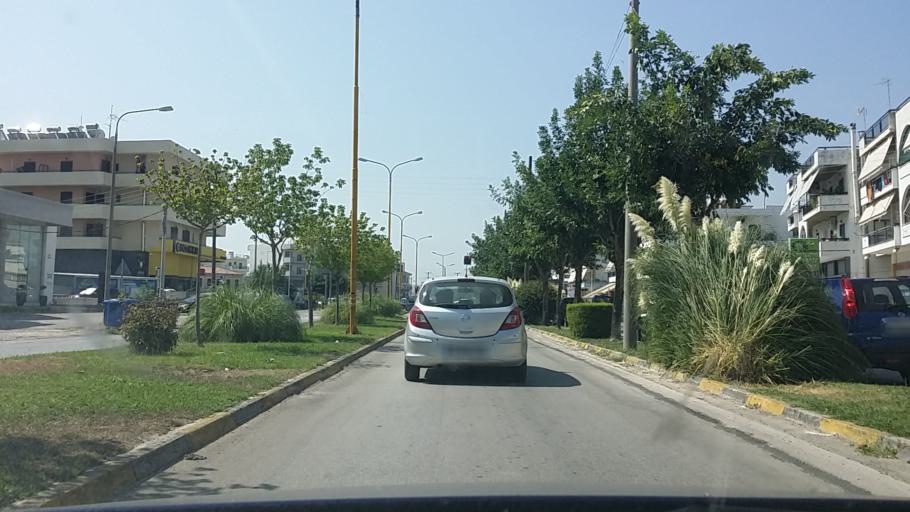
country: GR
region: Epirus
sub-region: Nomos Artas
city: Arta
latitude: 39.1551
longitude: 20.9785
